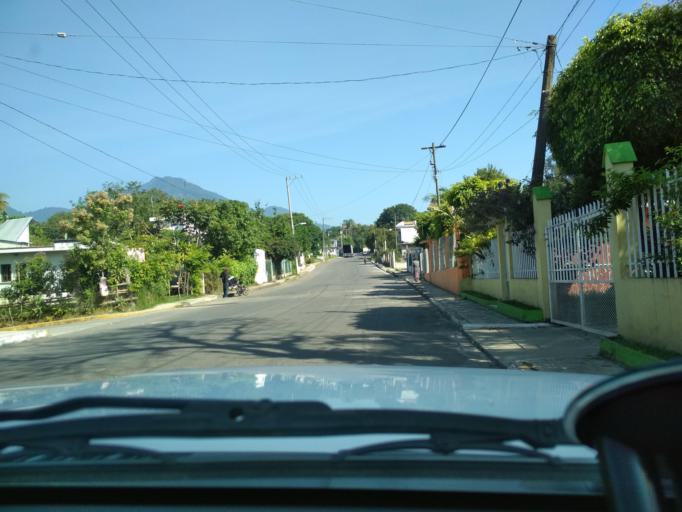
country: MX
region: Veracruz
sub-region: Chocaman
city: San Jose Neria
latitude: 19.0018
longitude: -97.0039
